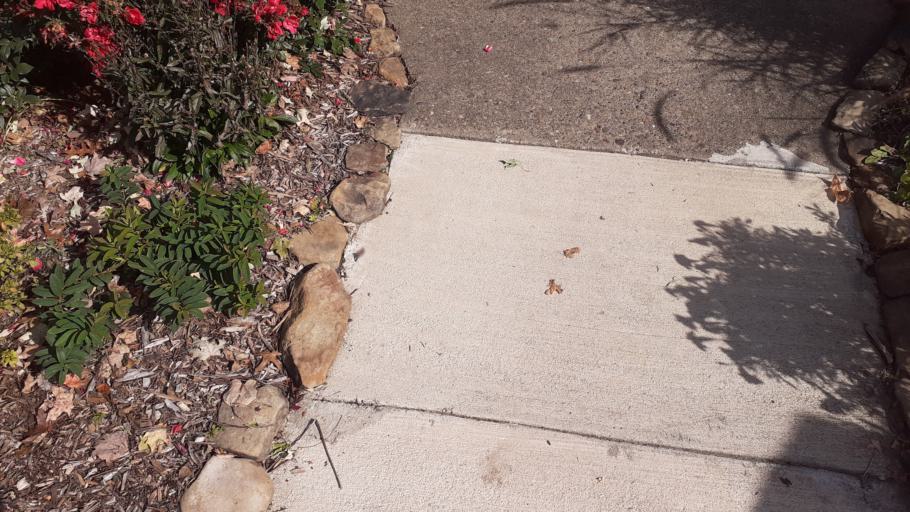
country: US
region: West Virginia
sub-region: Kanawha County
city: South Charleston
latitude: 38.3649
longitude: -81.6936
